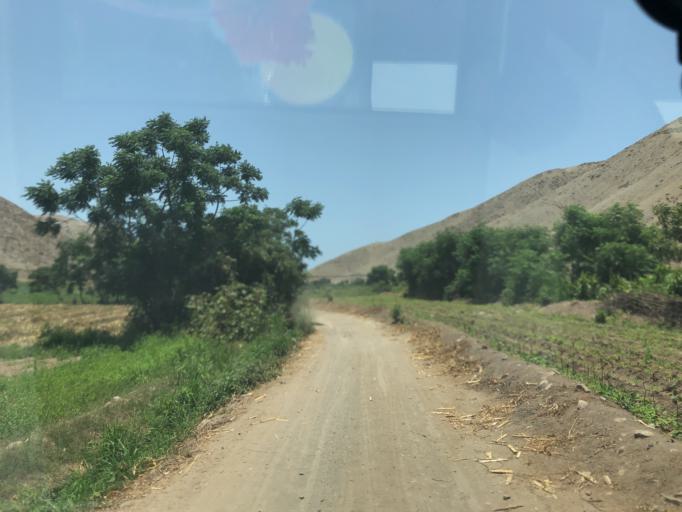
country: PE
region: Lima
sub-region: Provincia de Canete
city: Quilmana
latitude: -12.9841
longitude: -76.4329
